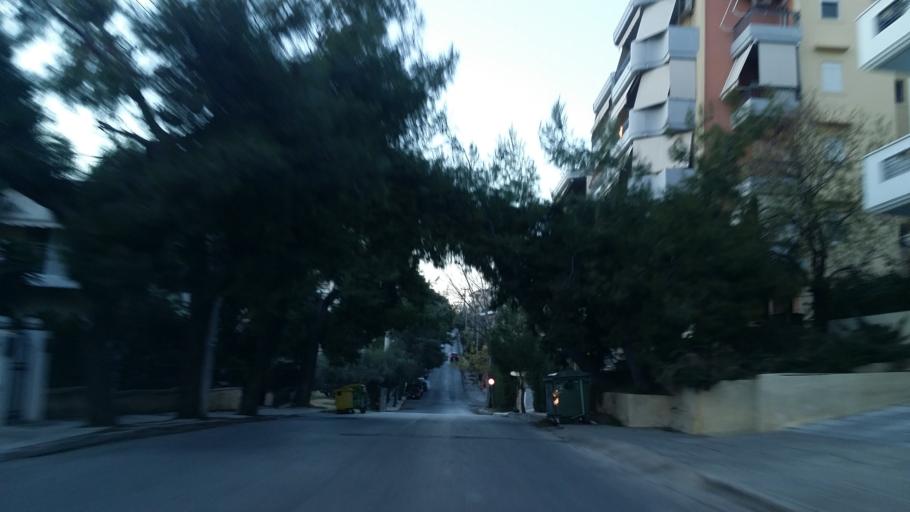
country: GR
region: Attica
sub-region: Nomarchia Athinas
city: Irakleio
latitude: 38.0534
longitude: 23.7642
